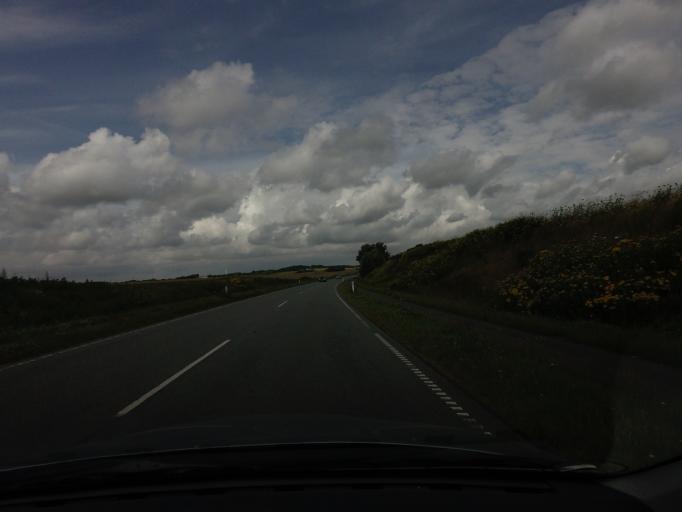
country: DK
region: North Denmark
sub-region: Hjorring Kommune
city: Tars
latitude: 57.3689
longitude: 10.1776
